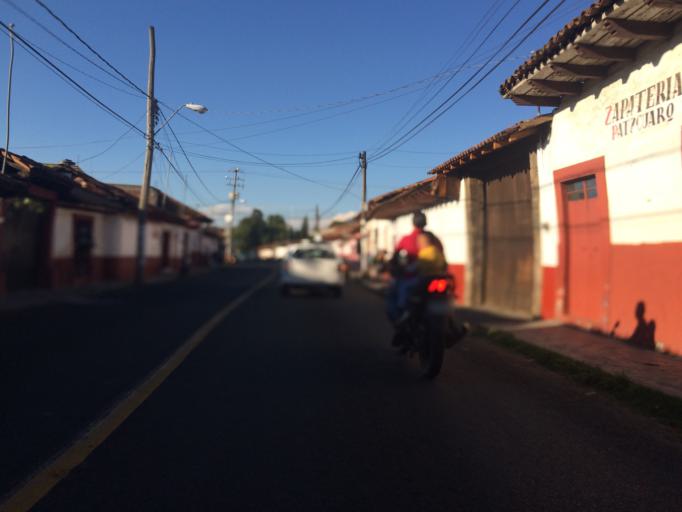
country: MX
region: Michoacan
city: Patzcuaro
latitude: 19.5114
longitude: -101.6127
